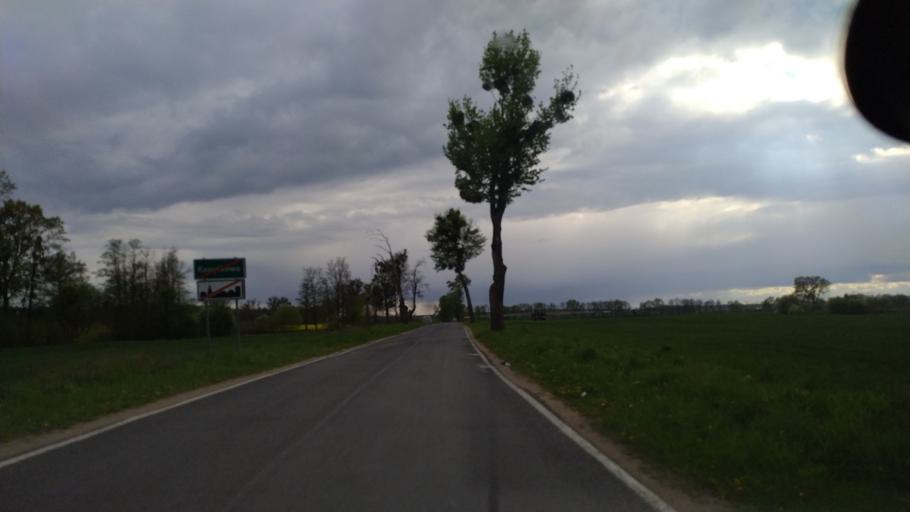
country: PL
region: Pomeranian Voivodeship
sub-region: Powiat starogardzki
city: Smetowo Graniczne
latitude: 53.7333
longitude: 18.6464
